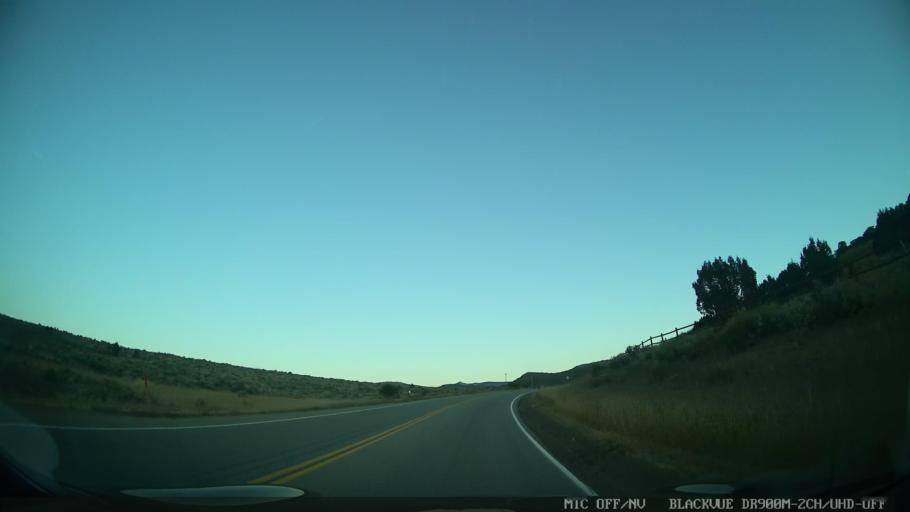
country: US
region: Colorado
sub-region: Eagle County
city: Edwards
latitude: 39.7057
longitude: -106.6830
